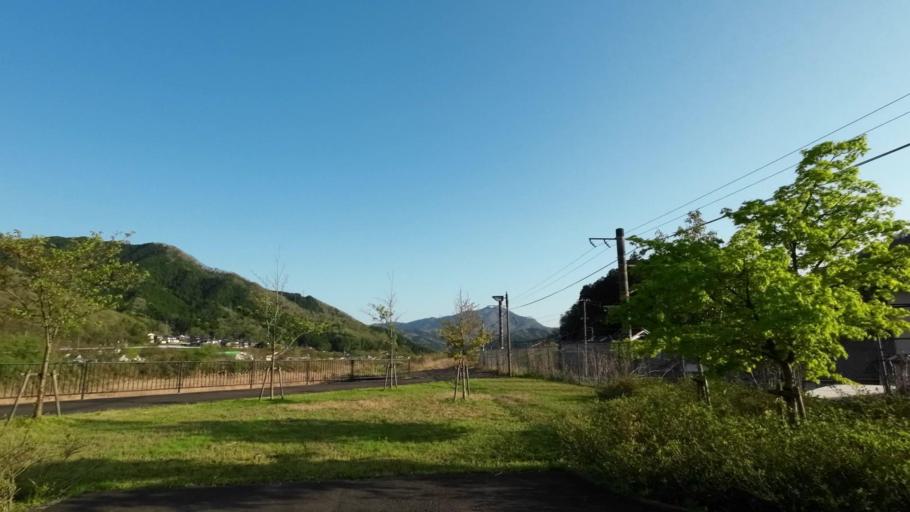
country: JP
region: Hyogo
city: Toyooka
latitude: 35.3842
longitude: 134.8141
